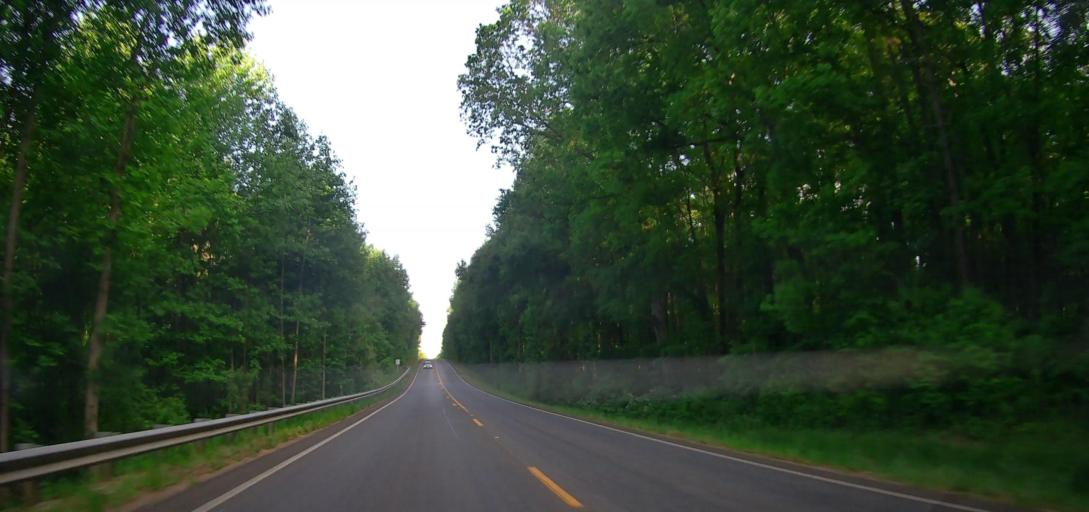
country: US
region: Georgia
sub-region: Putnam County
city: Eatonton
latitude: 33.3676
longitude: -83.5295
